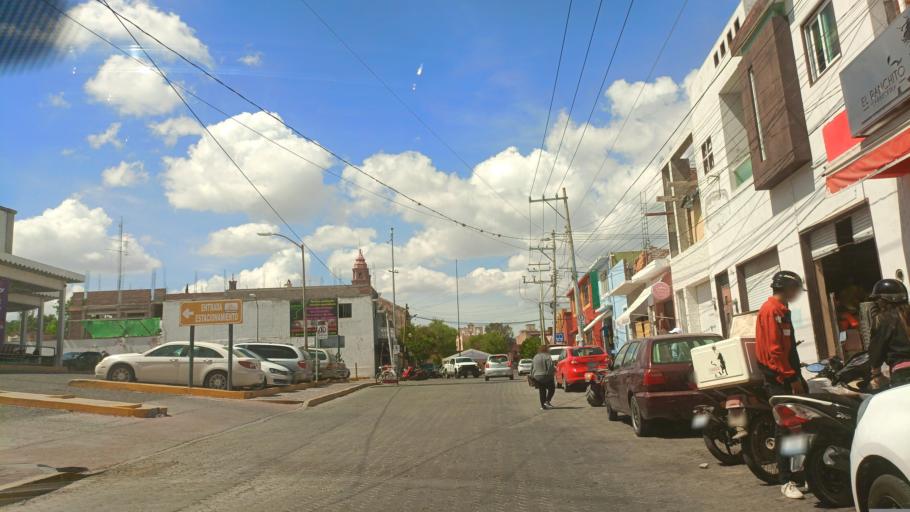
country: MX
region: Guanajuato
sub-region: San Luis de la Paz
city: San Luis de la Paz
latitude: 21.3007
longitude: -100.5141
